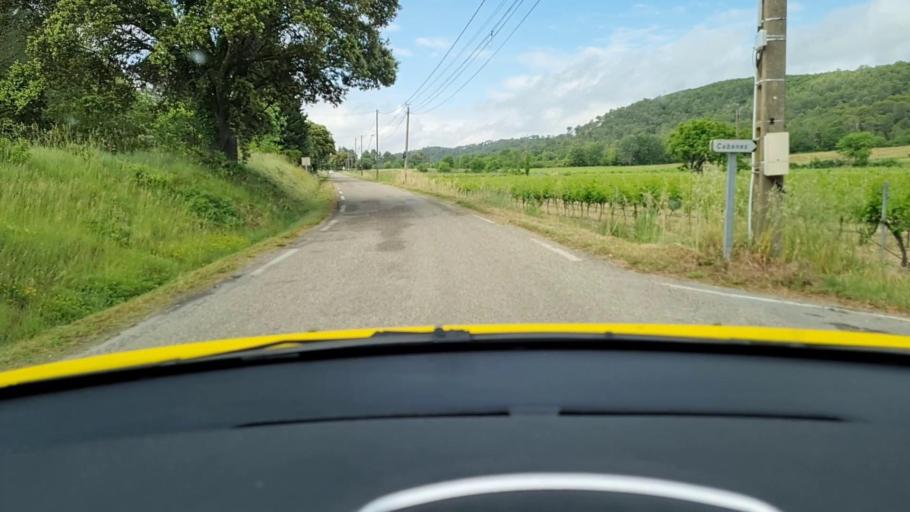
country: FR
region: Languedoc-Roussillon
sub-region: Departement du Gard
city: Quissac
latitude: 43.8549
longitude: 4.0122
